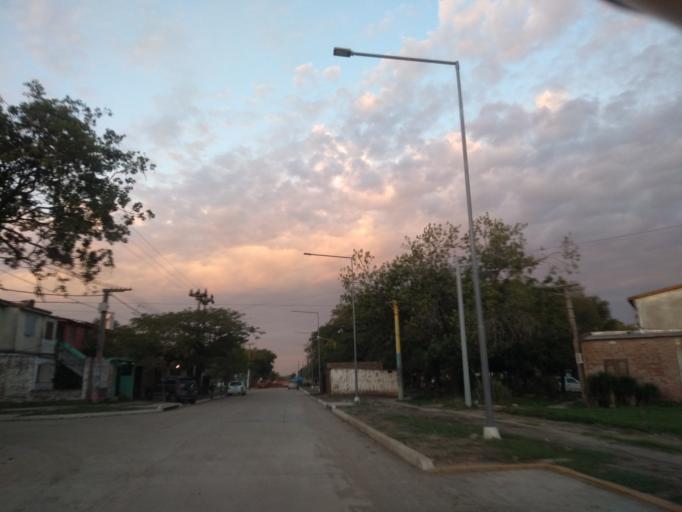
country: AR
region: Chaco
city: Resistencia
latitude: -27.4847
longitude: -58.9879
